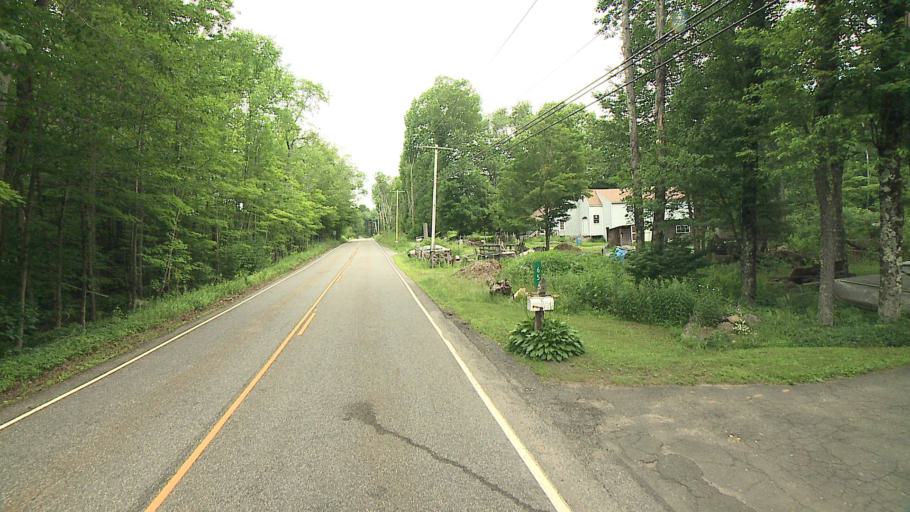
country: US
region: Connecticut
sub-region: Litchfield County
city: Winsted
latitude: 41.9948
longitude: -72.9999
